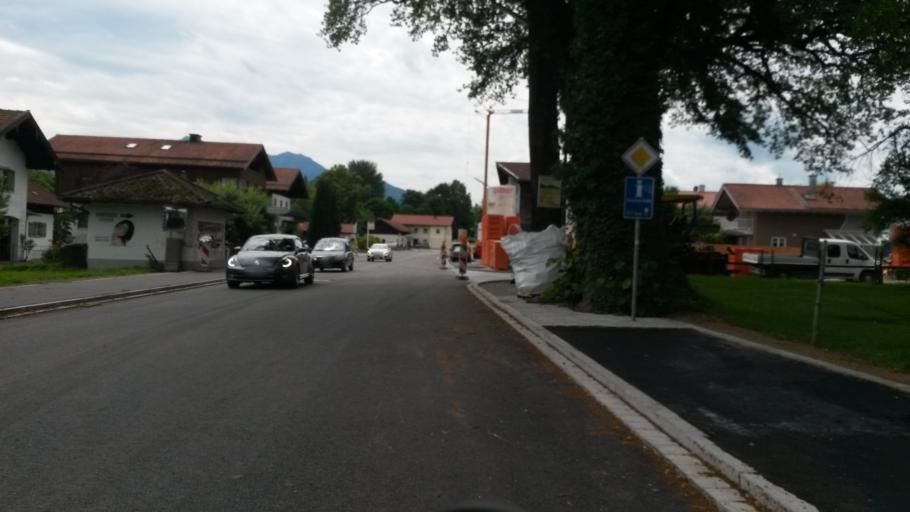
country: DE
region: Bavaria
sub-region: Upper Bavaria
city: Ubersee
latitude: 47.8354
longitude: 12.4883
